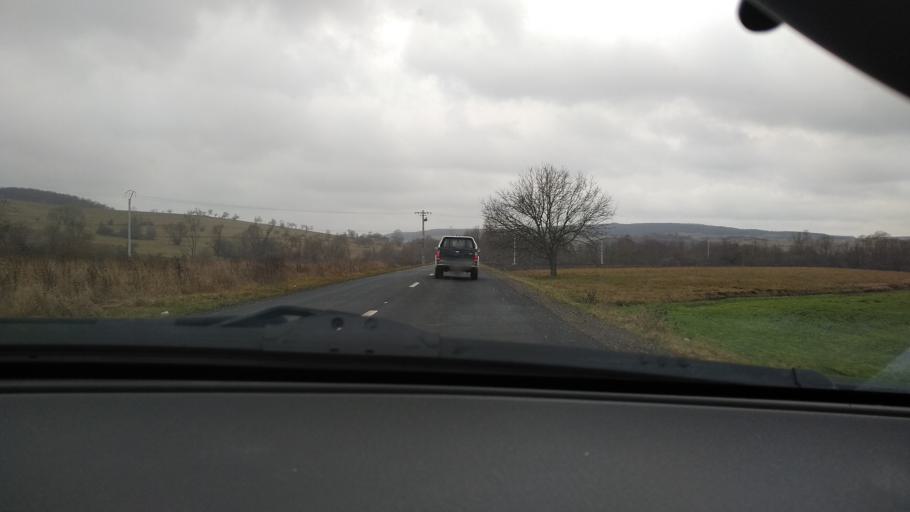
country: RO
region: Mures
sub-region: Comuna Magherani
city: Magherani
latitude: 46.5585
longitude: 24.8909
